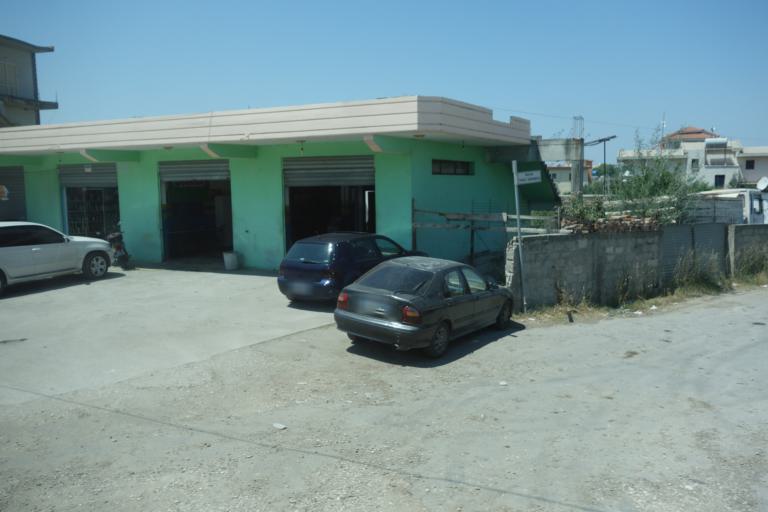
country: AL
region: Fier
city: Fier-Cifci
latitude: 40.7180
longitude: 19.5633
